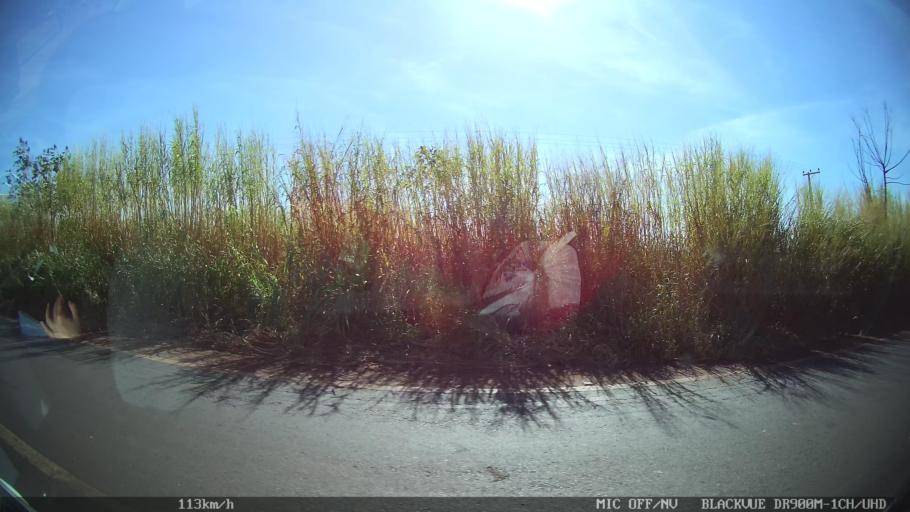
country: BR
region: Sao Paulo
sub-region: Barretos
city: Barretos
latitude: -20.4832
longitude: -48.5084
